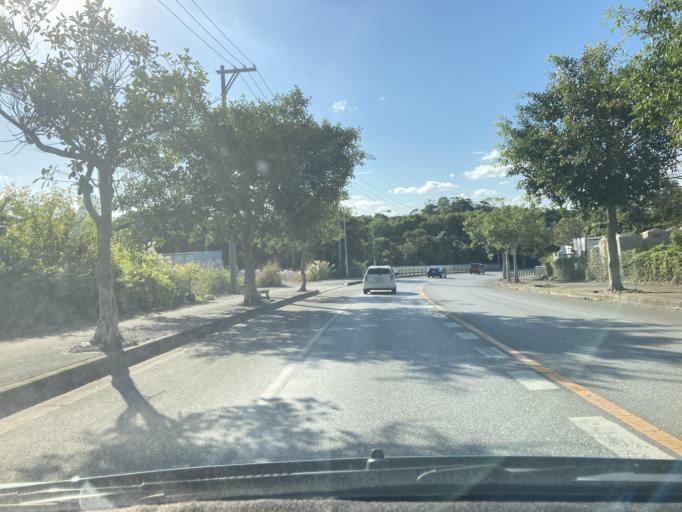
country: JP
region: Okinawa
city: Gushikawa
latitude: 26.3689
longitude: 127.8321
